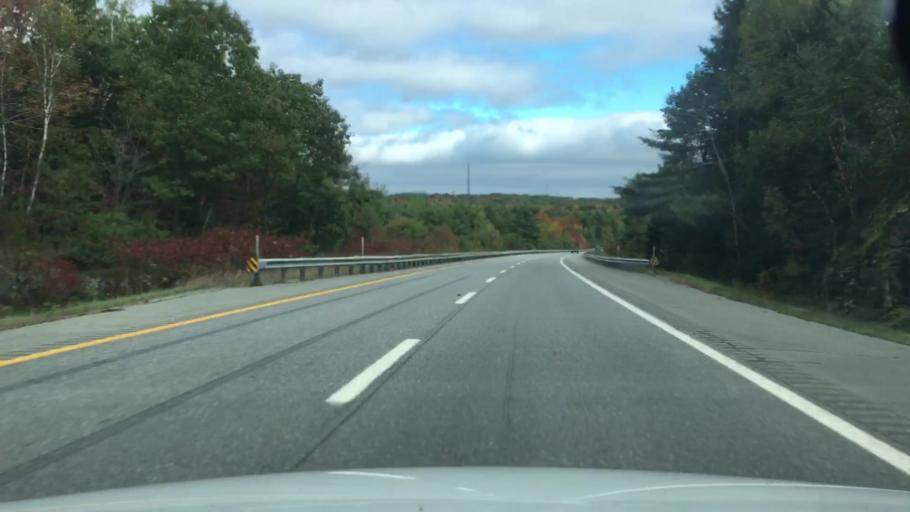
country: US
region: Maine
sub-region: Penobscot County
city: Carmel
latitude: 44.7718
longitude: -69.0067
